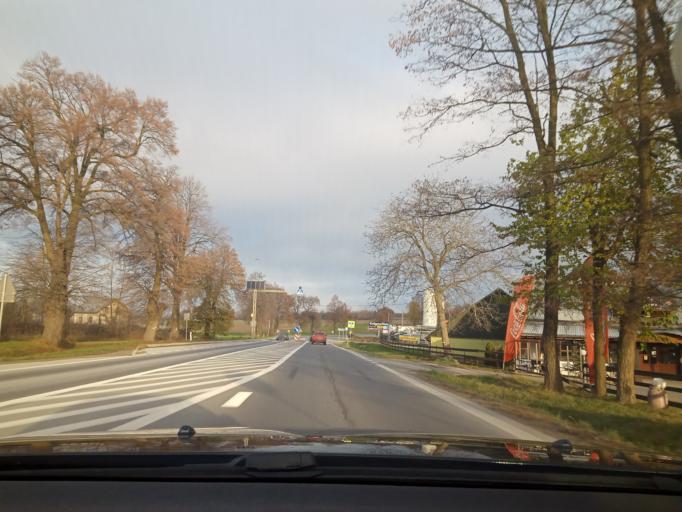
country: PL
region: Lesser Poland Voivodeship
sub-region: Powiat miechowski
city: Miechow
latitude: 50.3223
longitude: 20.0354
